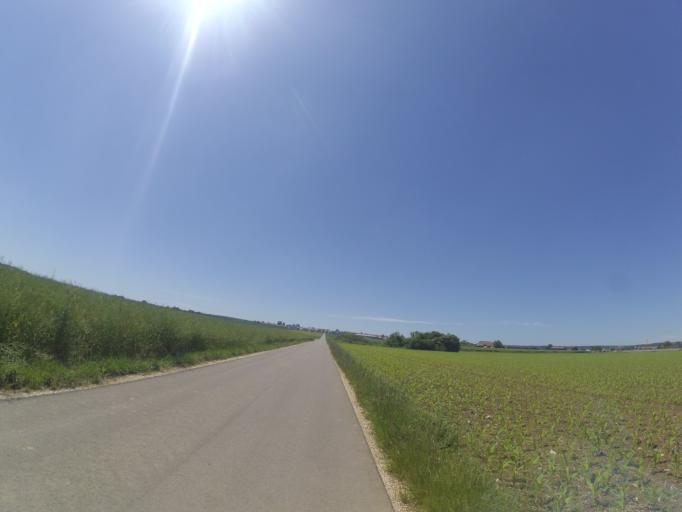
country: DE
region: Baden-Wuerttemberg
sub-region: Tuebingen Region
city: Blaubeuren
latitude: 48.4698
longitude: 9.8499
